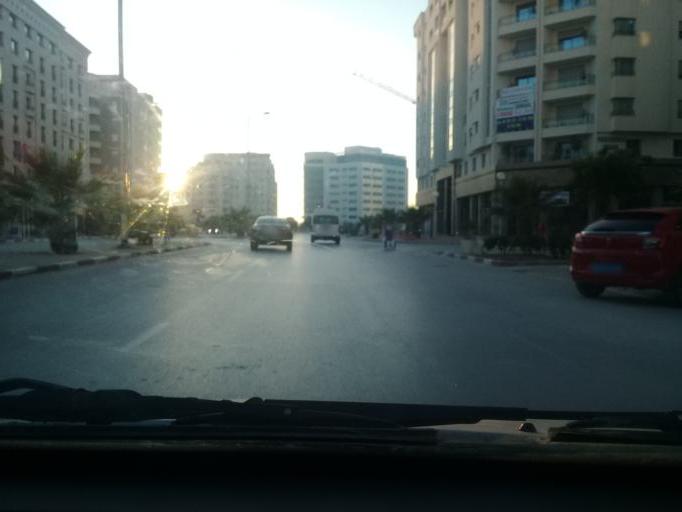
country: TN
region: Tunis
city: La Goulette
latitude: 36.8476
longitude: 10.2773
